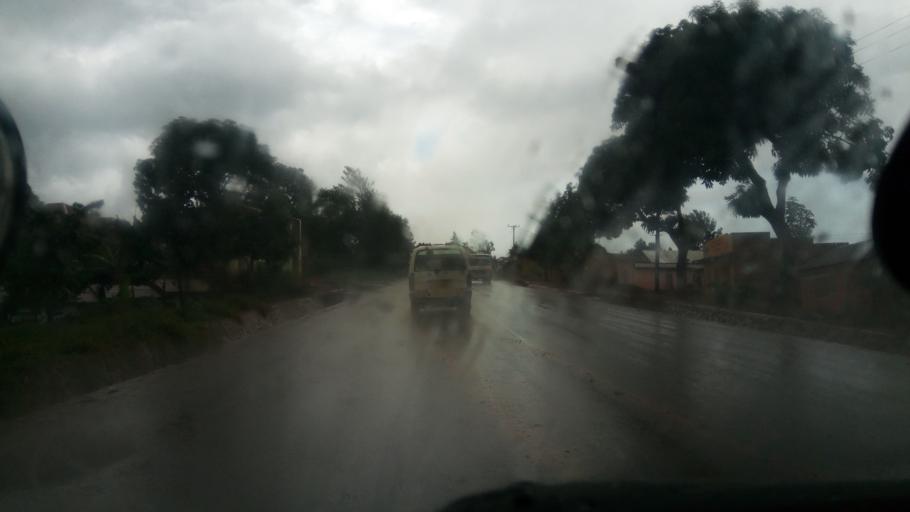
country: UG
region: Central Region
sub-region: Wakiso District
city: Wakiso
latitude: 0.4057
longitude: 32.4712
